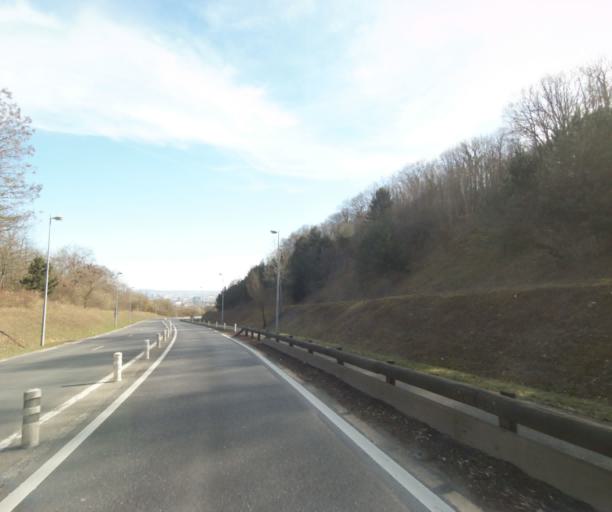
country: FR
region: Lorraine
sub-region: Departement de Meurthe-et-Moselle
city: Laxou
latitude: 48.6848
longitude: 6.1344
